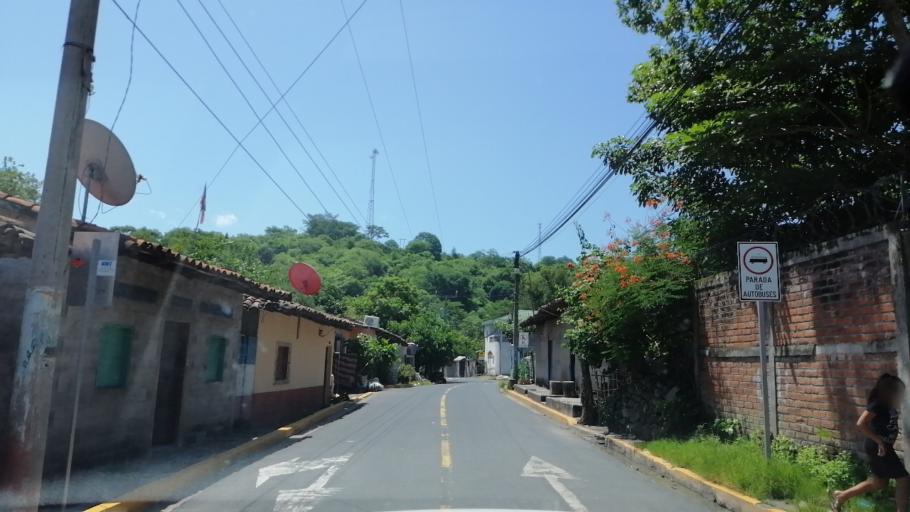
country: SV
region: San Miguel
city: Sesori
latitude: 13.8100
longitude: -88.4068
